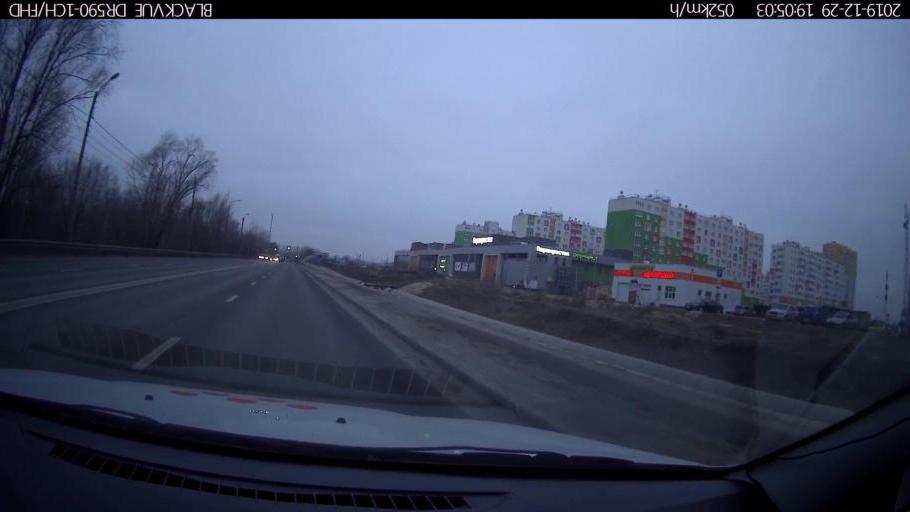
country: RU
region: Nizjnij Novgorod
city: Nizhniy Novgorod
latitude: 56.3409
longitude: 43.9093
